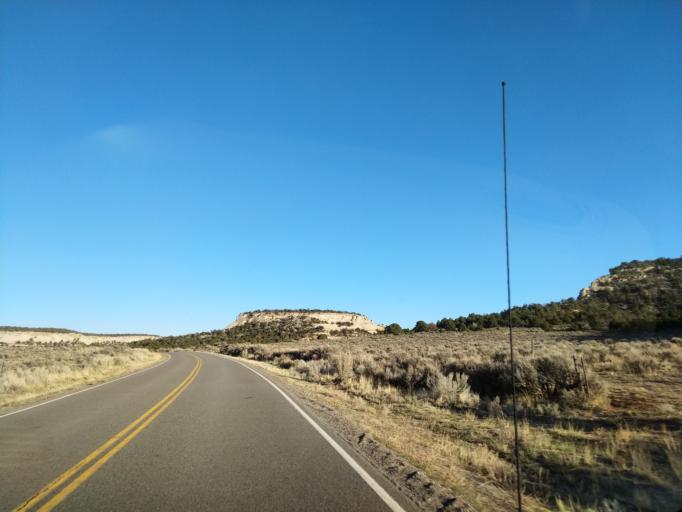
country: US
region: Colorado
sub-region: Mesa County
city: Fruita
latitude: 38.9847
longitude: -108.8099
